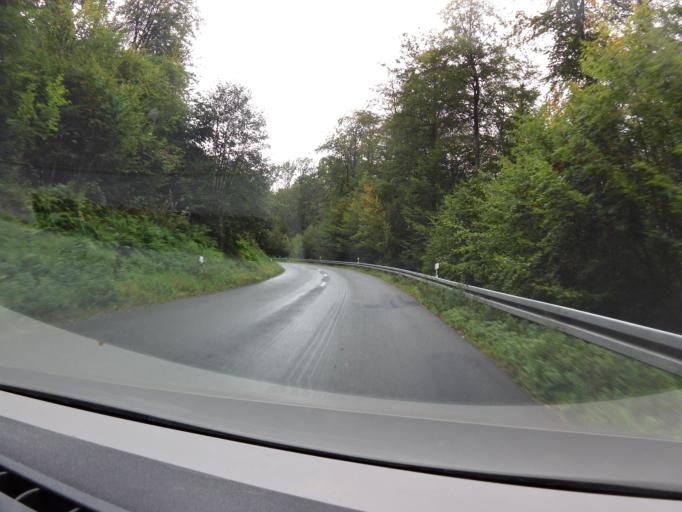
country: DE
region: Lower Saxony
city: Furstenberg
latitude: 51.7199
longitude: 9.4093
